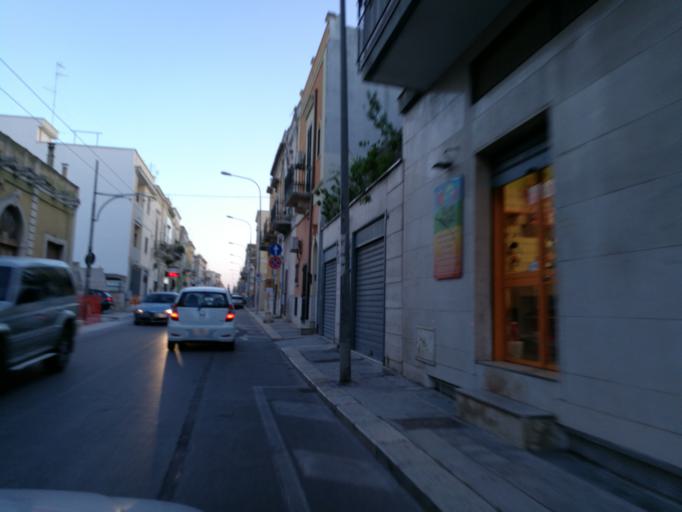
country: IT
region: Apulia
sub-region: Provincia di Bari
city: Valenzano
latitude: 41.0657
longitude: 16.8686
